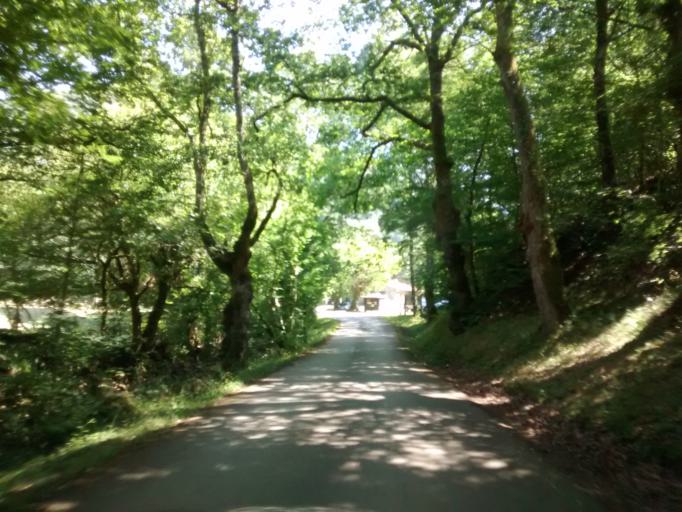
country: ES
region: Cantabria
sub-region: Provincia de Cantabria
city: Ruente
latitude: 43.2357
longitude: -4.2210
